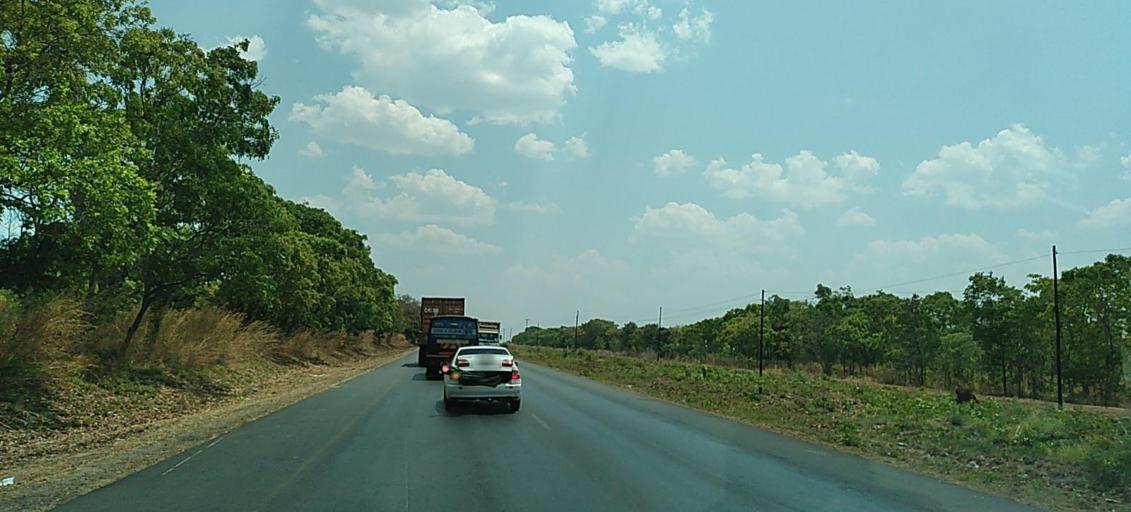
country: ZM
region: Central
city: Kabwe
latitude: -14.3323
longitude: 28.5355
